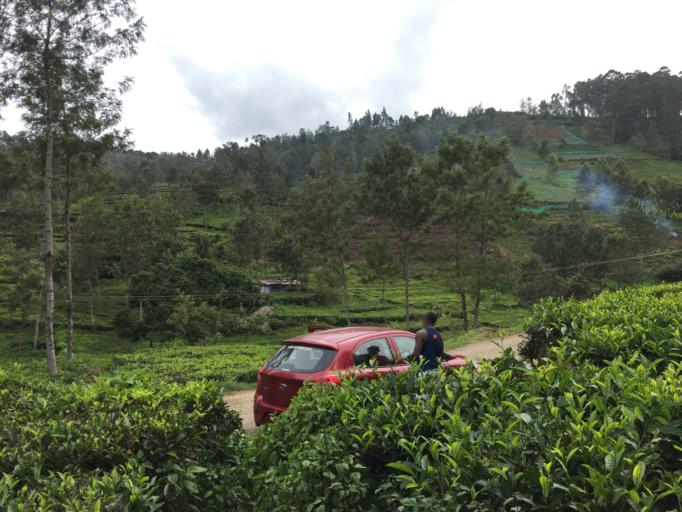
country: IN
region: Tamil Nadu
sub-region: Nilgiri
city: Kotagiri
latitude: 11.4598
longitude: 76.8585
